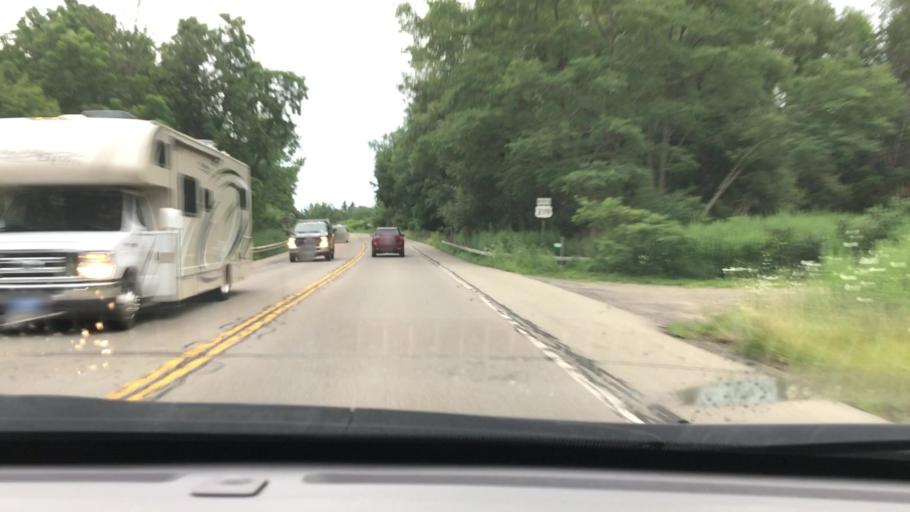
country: US
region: New York
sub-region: Erie County
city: Springville
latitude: 42.4198
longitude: -78.6936
